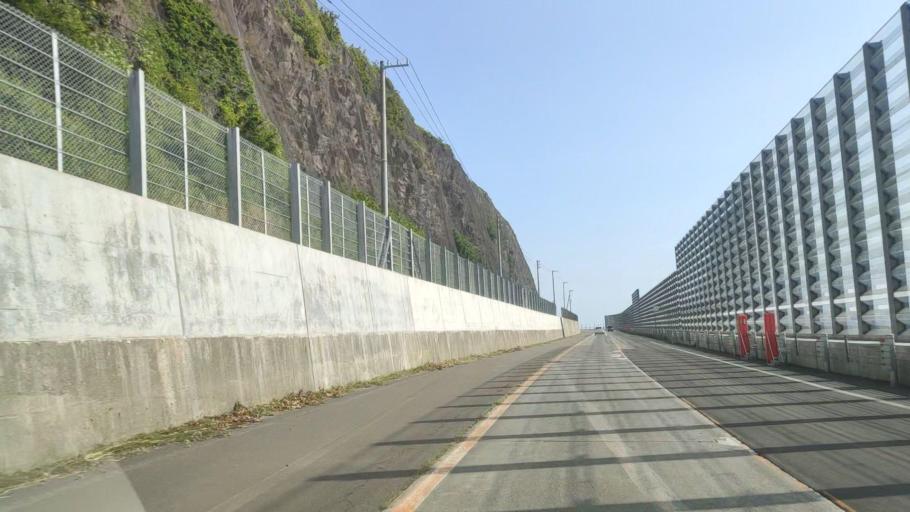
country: JP
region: Hokkaido
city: Rumoi
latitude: 43.6565
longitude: 141.3504
